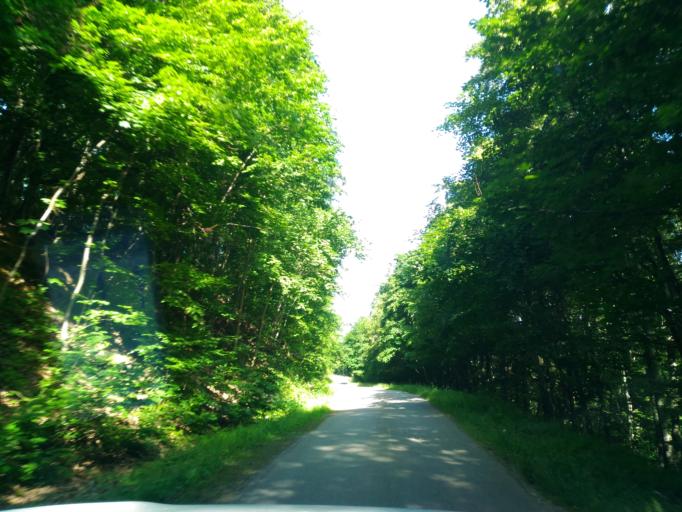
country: HU
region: Baranya
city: Hosszuheteny
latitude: 46.2184
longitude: 18.3518
